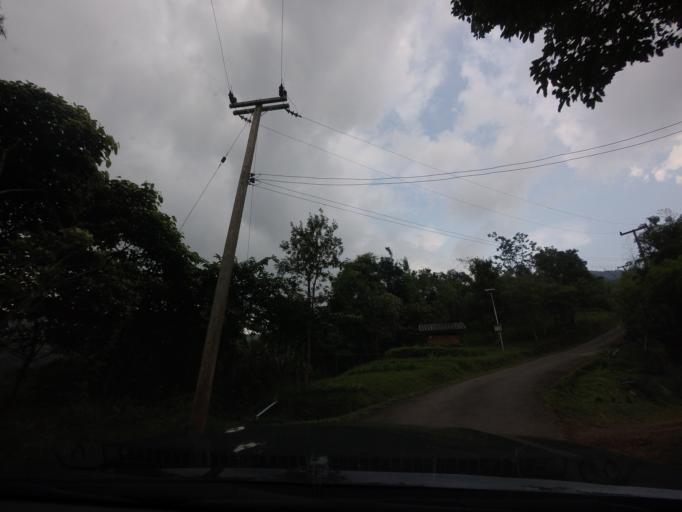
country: TH
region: Nan
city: Bo Kluea
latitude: 19.3501
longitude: 101.1798
